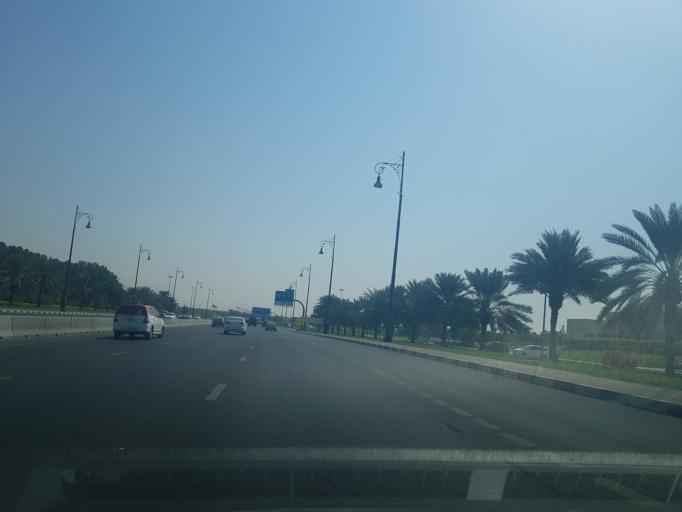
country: AE
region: Ash Shariqah
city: Sharjah
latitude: 25.3185
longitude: 55.5133
